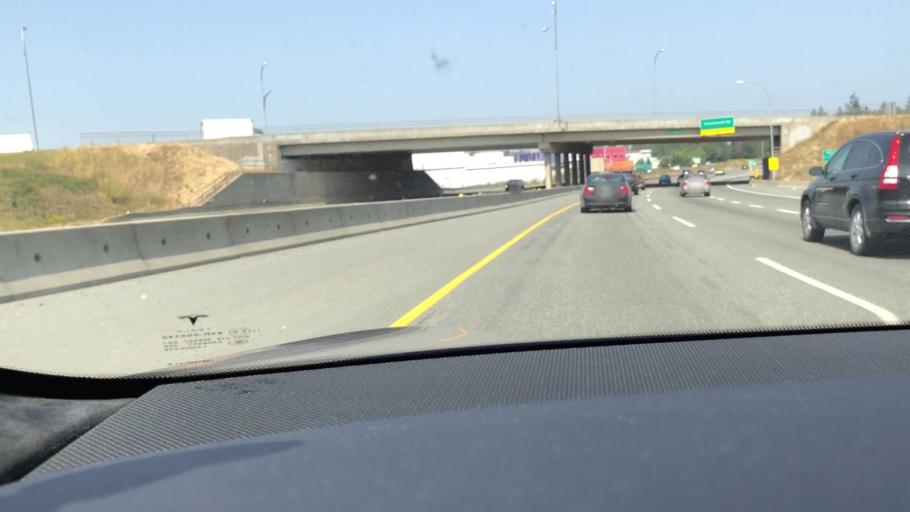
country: US
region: Washington
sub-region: Whatcom County
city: Sumas
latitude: 49.0374
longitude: -122.3367
